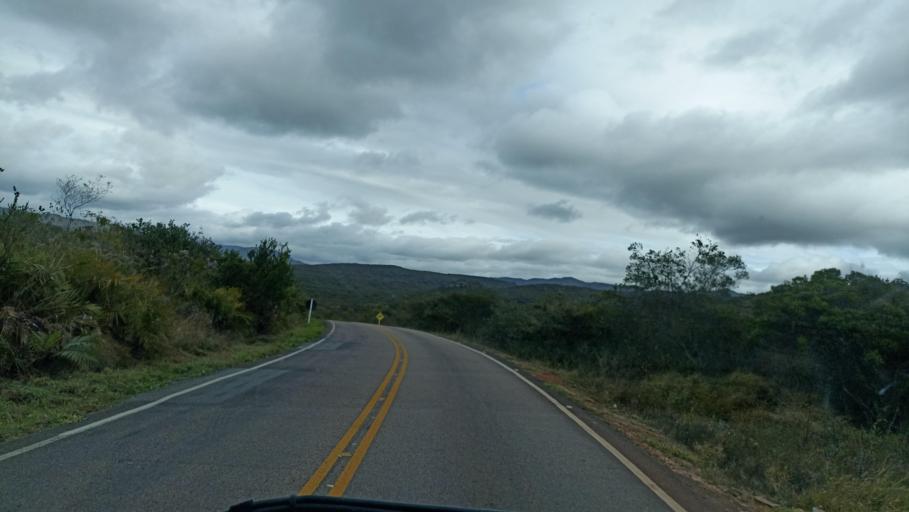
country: BR
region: Bahia
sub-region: Andarai
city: Vera Cruz
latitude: -12.9936
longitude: -41.3581
